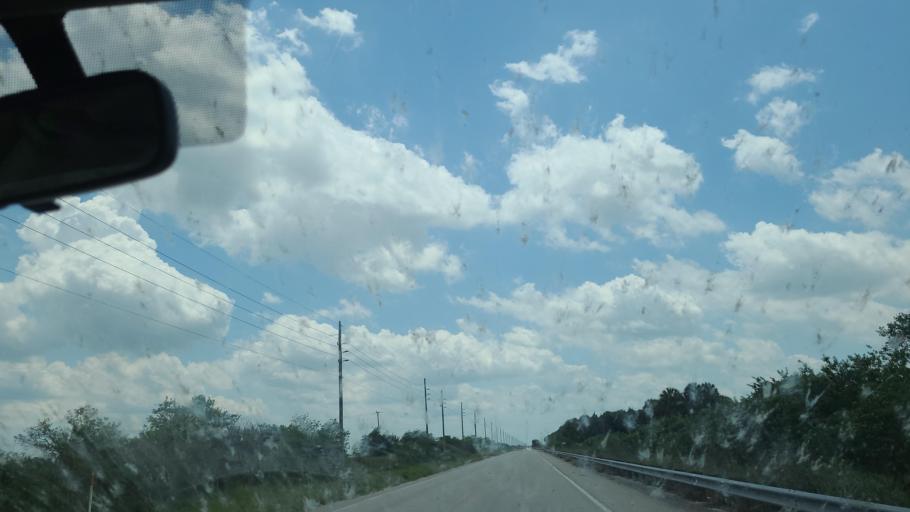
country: US
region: Florida
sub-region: Glades County
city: Buckhead Ridge
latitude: 27.2002
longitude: -81.0944
